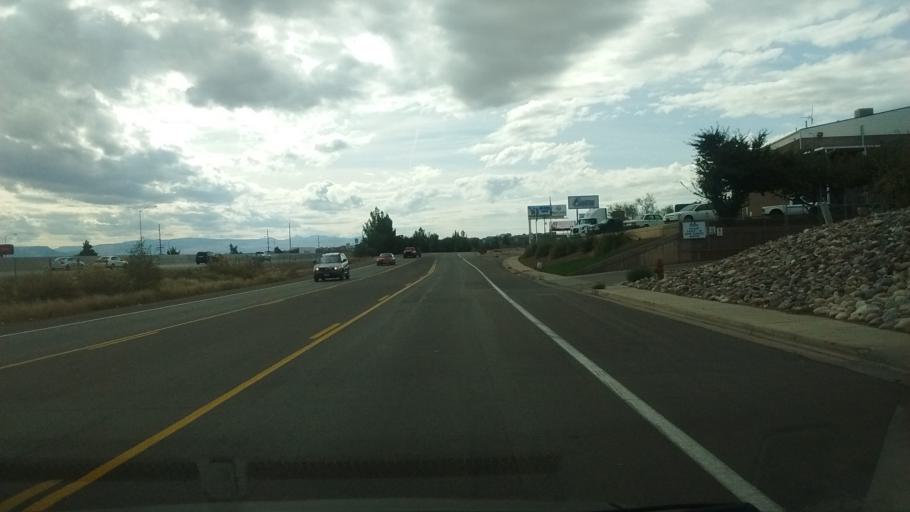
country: US
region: Utah
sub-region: Washington County
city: Washington
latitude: 37.1261
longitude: -113.5305
